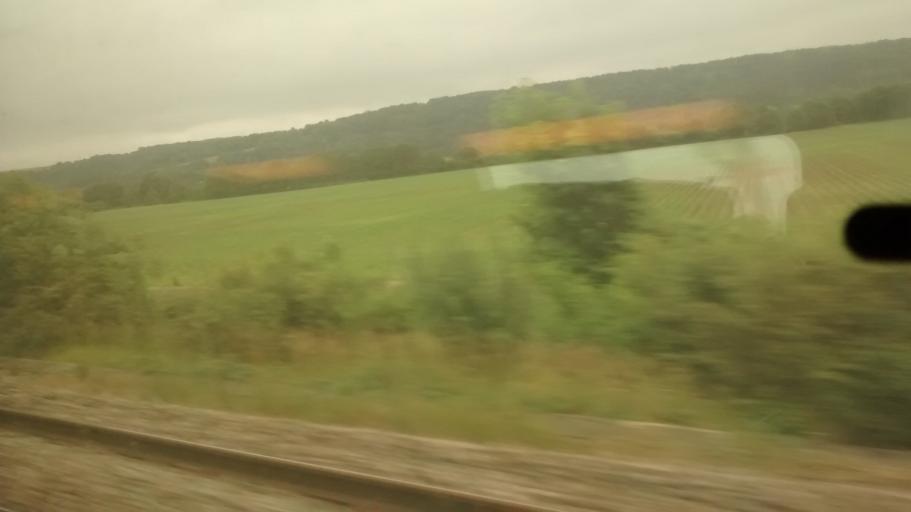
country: FR
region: Bourgogne
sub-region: Departement de l'Yonne
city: Malay-le-Grand
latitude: 48.1742
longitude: 3.3684
